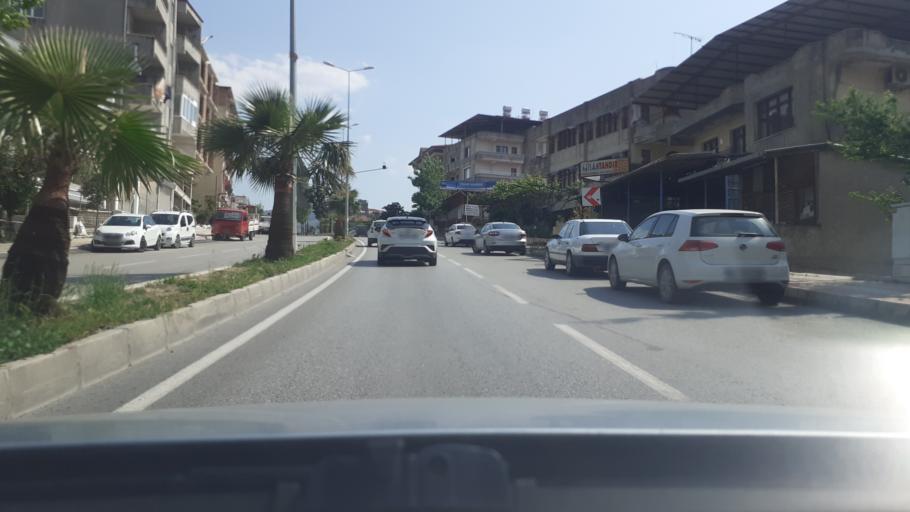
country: TR
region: Hatay
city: Gumusgoze
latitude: 36.1434
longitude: 36.1412
